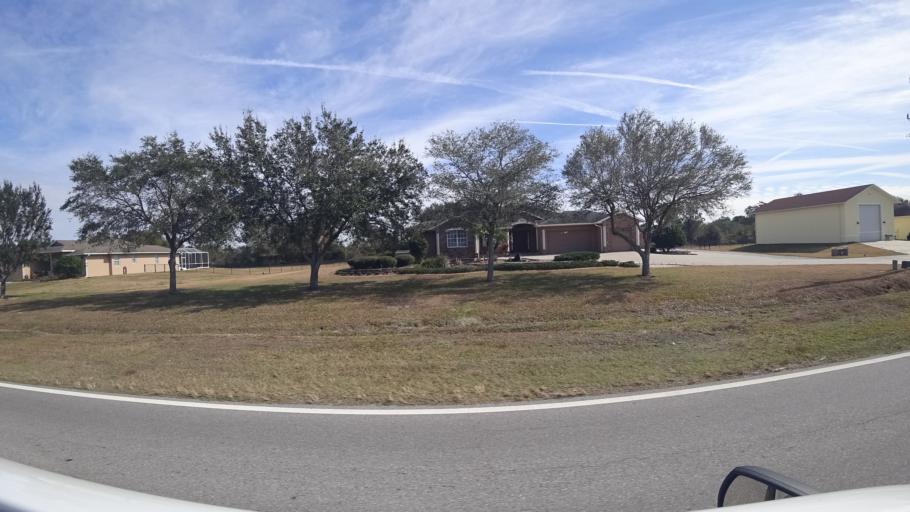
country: US
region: Florida
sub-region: Manatee County
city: Ellenton
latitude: 27.5341
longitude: -82.3688
